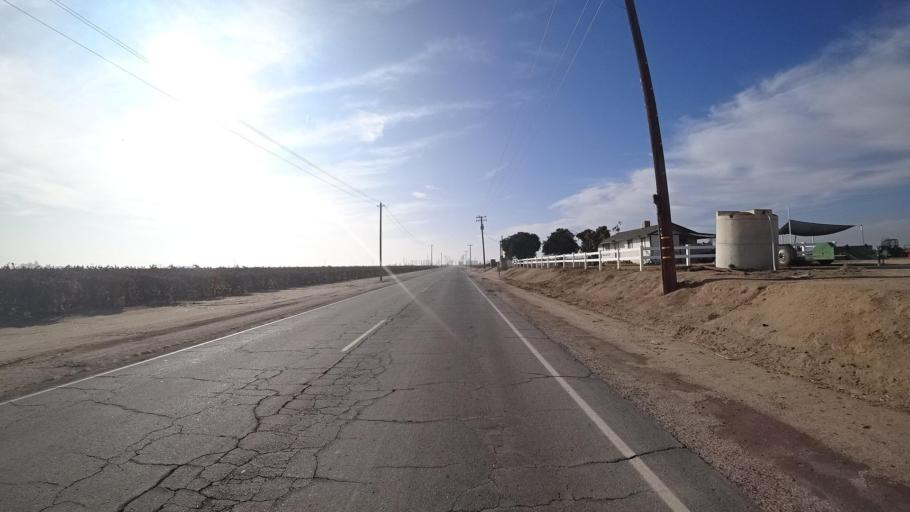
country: US
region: California
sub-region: Kern County
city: McFarland
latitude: 35.6127
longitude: -119.2044
